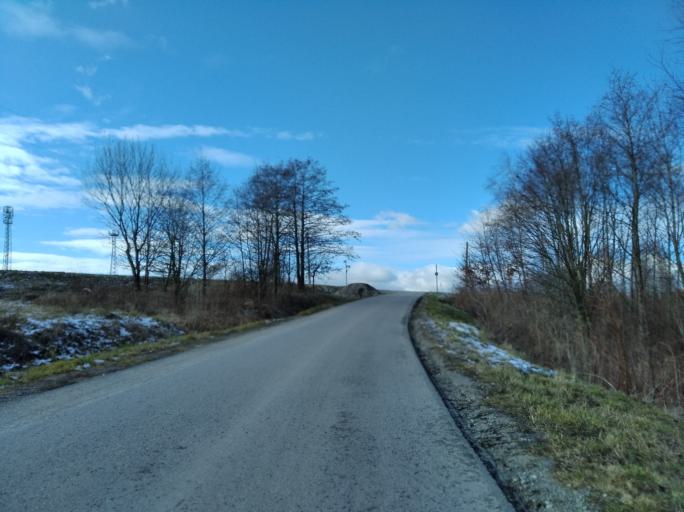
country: PL
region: Subcarpathian Voivodeship
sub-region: Powiat ropczycko-sedziszowski
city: Wielopole Skrzynskie
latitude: 49.9148
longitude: 21.6381
